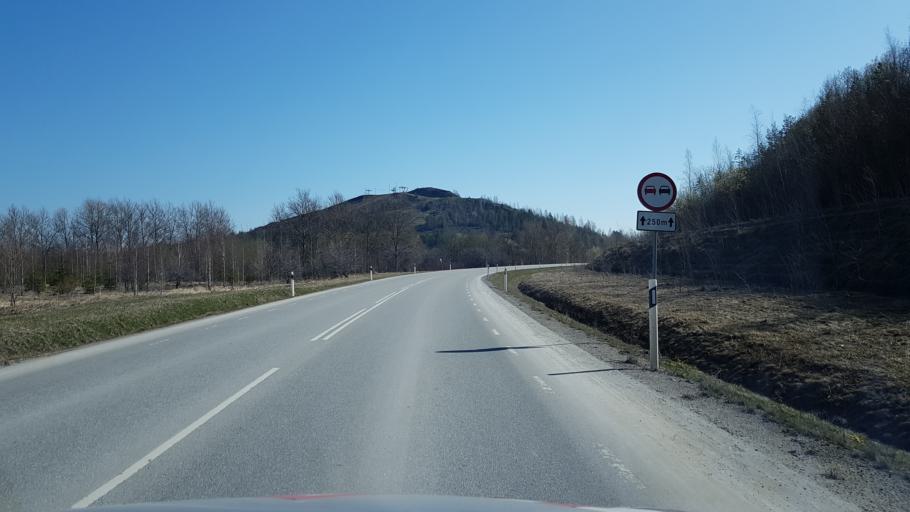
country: EE
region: Ida-Virumaa
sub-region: Kivioli linn
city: Kivioli
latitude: 59.3582
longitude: 26.9399
